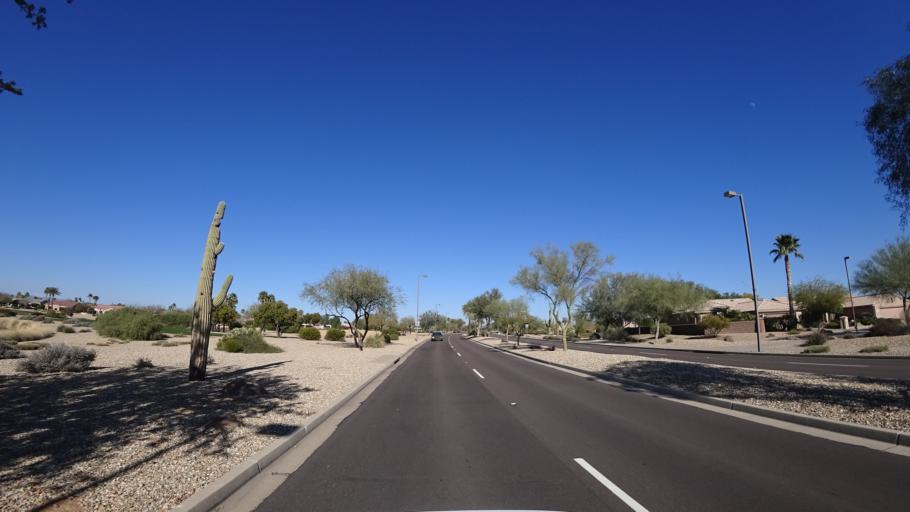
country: US
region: Arizona
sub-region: Maricopa County
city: Sun City West
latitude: 33.6601
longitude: -112.4014
